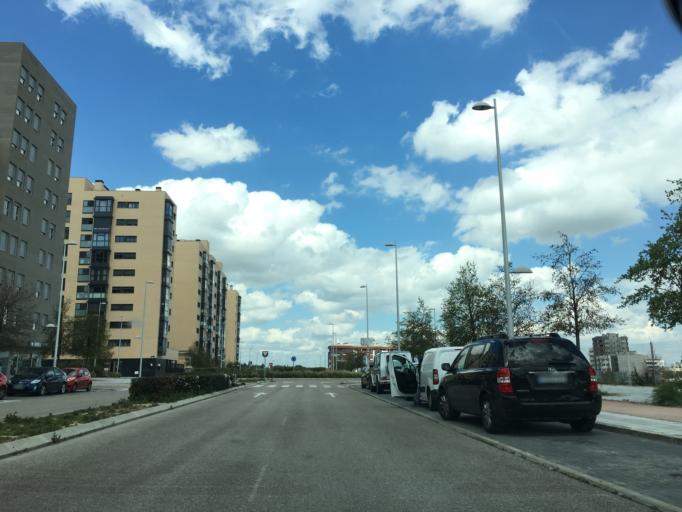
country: ES
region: Madrid
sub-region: Provincia de Madrid
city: Hortaleza
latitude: 40.4948
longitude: -3.6160
